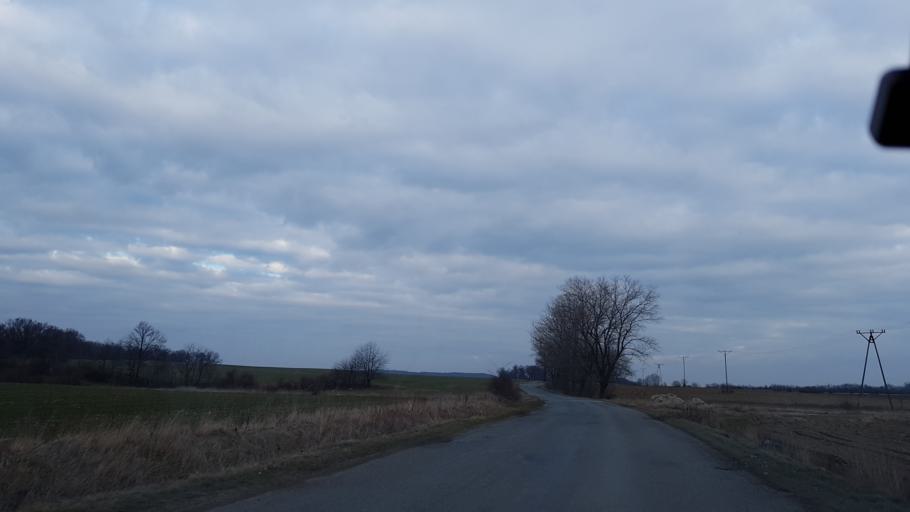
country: PL
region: Lower Silesian Voivodeship
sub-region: Powiat zabkowicki
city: Kamieniec Zabkowicki
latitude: 50.4995
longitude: 16.8433
